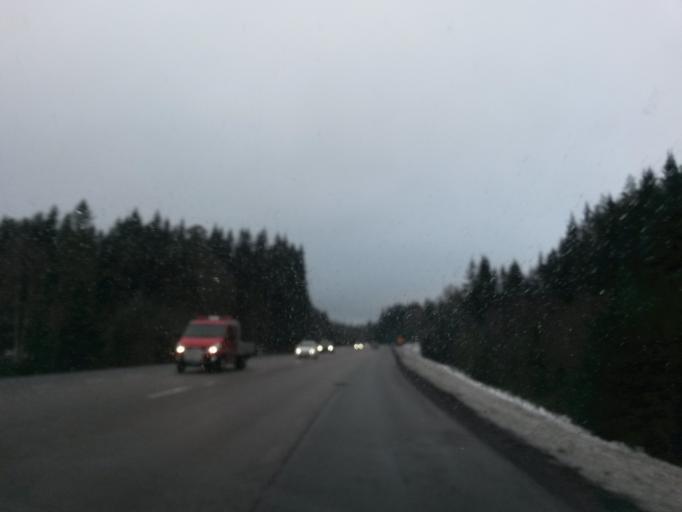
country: SE
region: Vaestra Goetaland
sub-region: Boras Kommun
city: Boras
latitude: 57.6641
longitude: 12.9187
